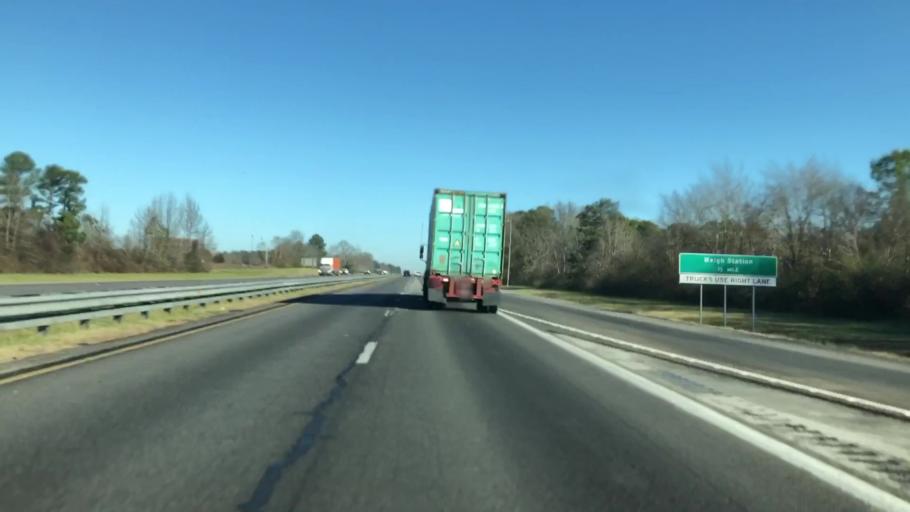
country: US
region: Alabama
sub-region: Limestone County
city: Athens
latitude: 34.8347
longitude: -86.9373
